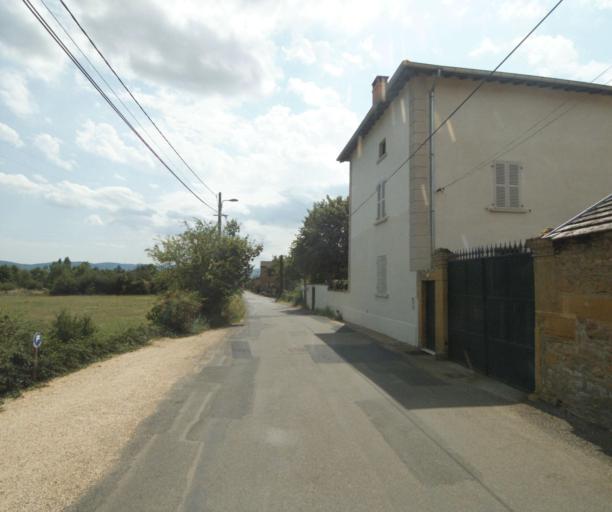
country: FR
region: Rhone-Alpes
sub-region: Departement du Rhone
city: Saint-Germain-Nuelles
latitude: 45.8565
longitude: 4.5987
